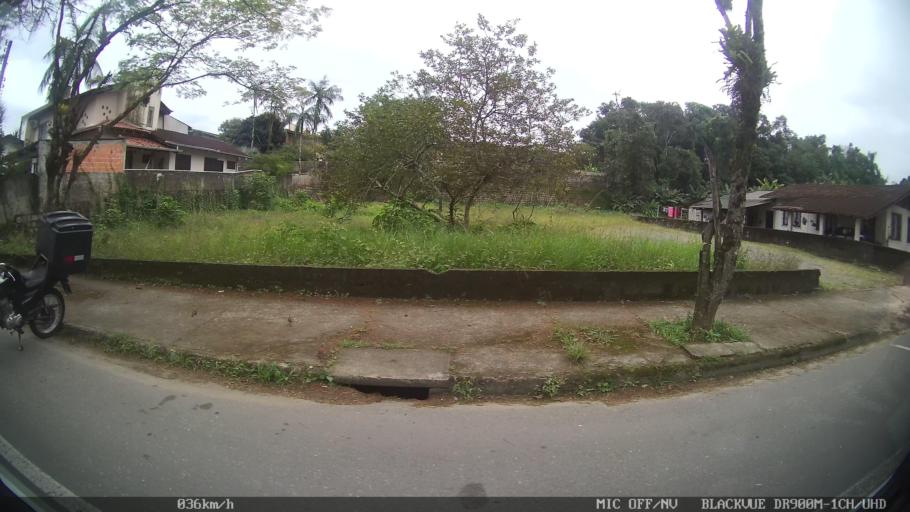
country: BR
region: Santa Catarina
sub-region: Joinville
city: Joinville
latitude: -26.2631
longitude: -48.8473
